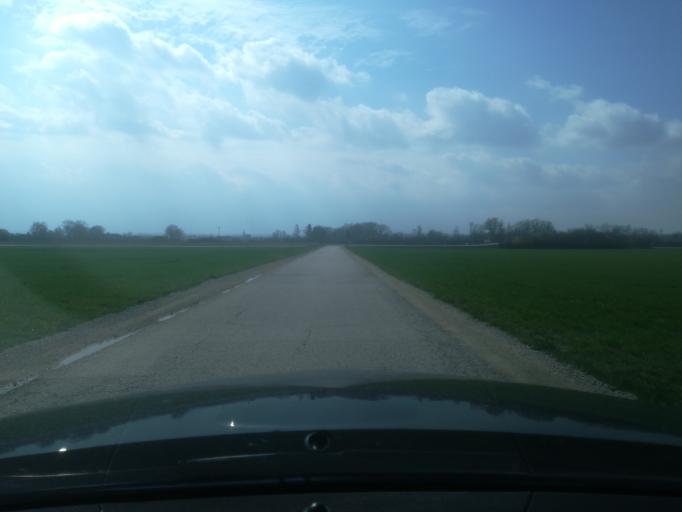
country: AT
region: Upper Austria
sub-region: Politischer Bezirk Perg
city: Perg
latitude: 48.2460
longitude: 14.6107
